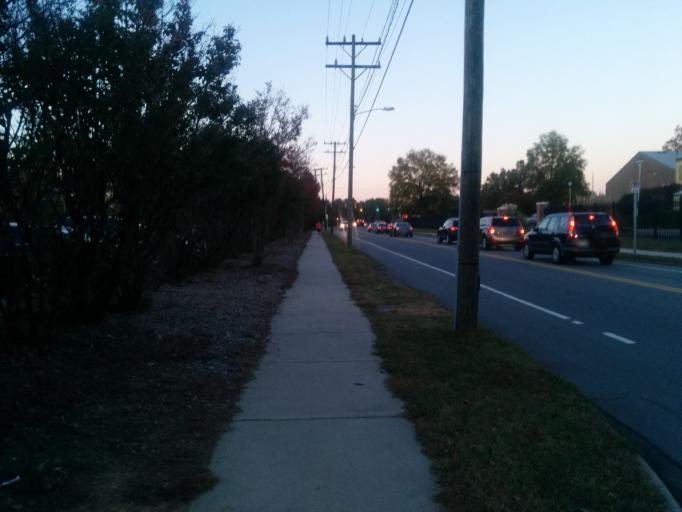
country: US
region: North Carolina
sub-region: Durham County
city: Durham
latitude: 36.0053
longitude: -78.9302
